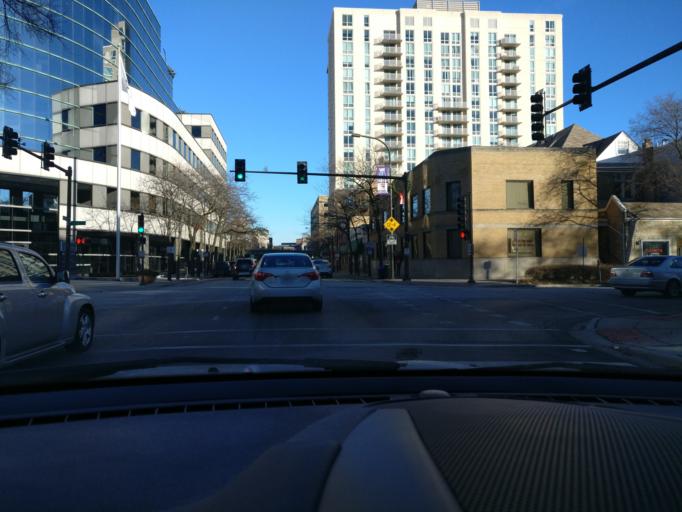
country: US
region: Illinois
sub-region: Cook County
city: Evanston
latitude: 42.0485
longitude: -87.6871
